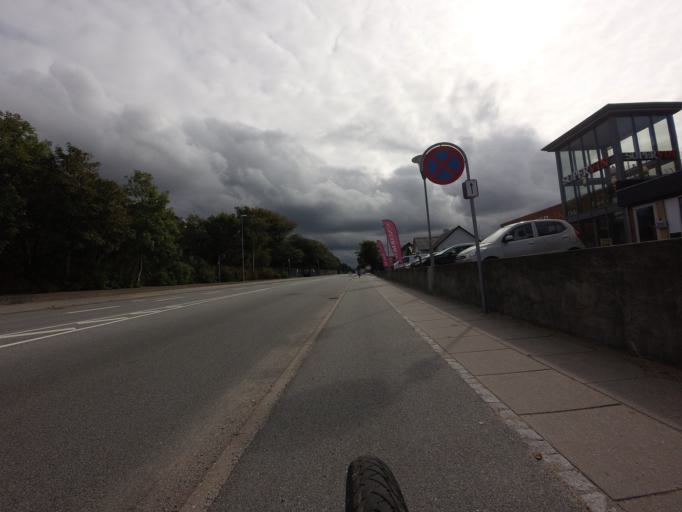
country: DK
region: North Denmark
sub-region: Hjorring Kommune
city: Hjorring
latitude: 57.4822
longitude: 9.9918
